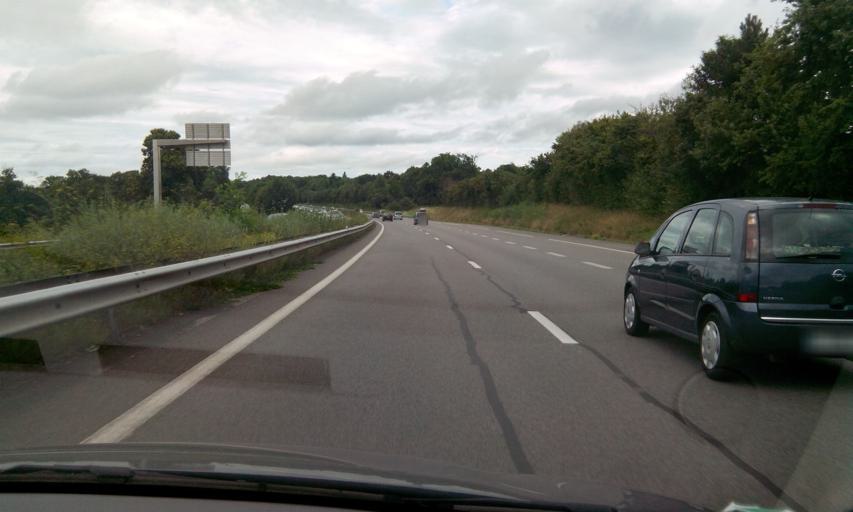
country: FR
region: Limousin
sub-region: Departement de la Correze
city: Uzerche
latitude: 45.4847
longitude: 1.5289
